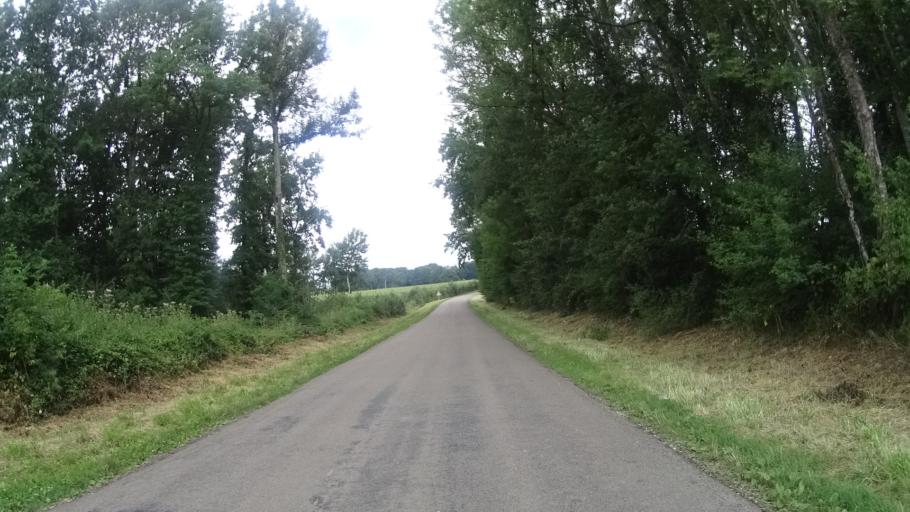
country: FR
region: Champagne-Ardenne
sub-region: Departement de l'Aube
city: Ervy-le-Chatel
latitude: 48.0846
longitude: 3.9591
